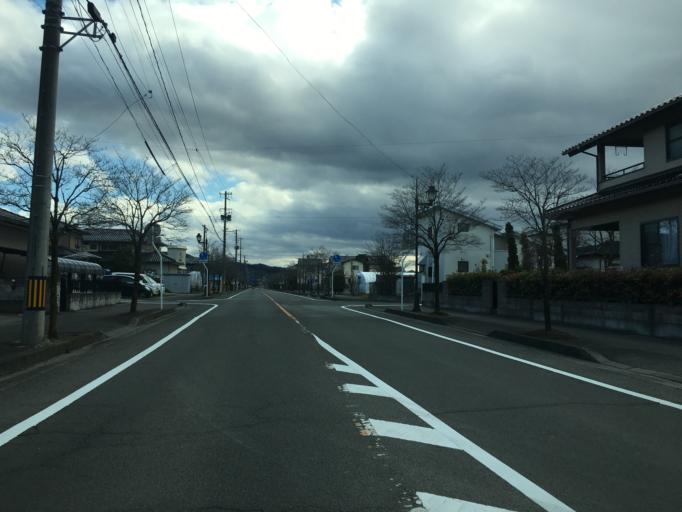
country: JP
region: Fukushima
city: Yanagawamachi-saiwaicho
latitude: 37.8508
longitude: 140.6005
